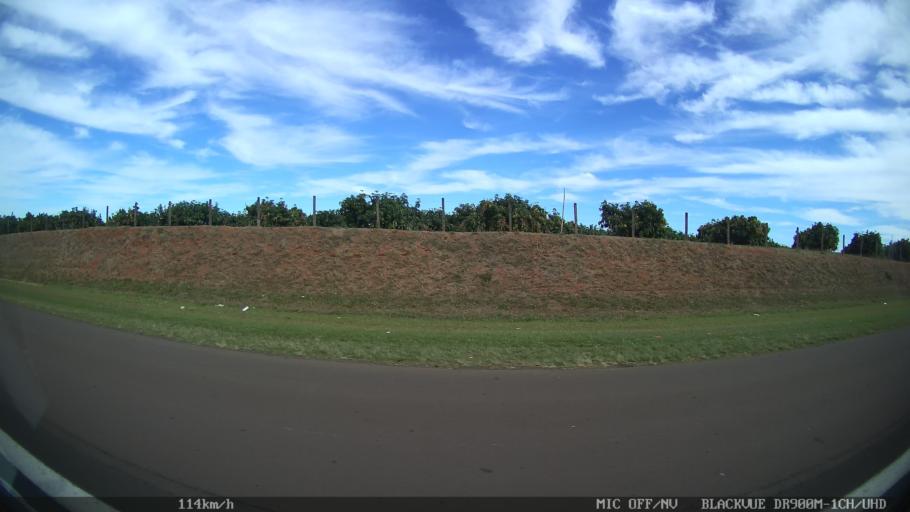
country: BR
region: Sao Paulo
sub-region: Taquaritinga
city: Taquaritinga
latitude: -21.4727
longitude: -48.6031
